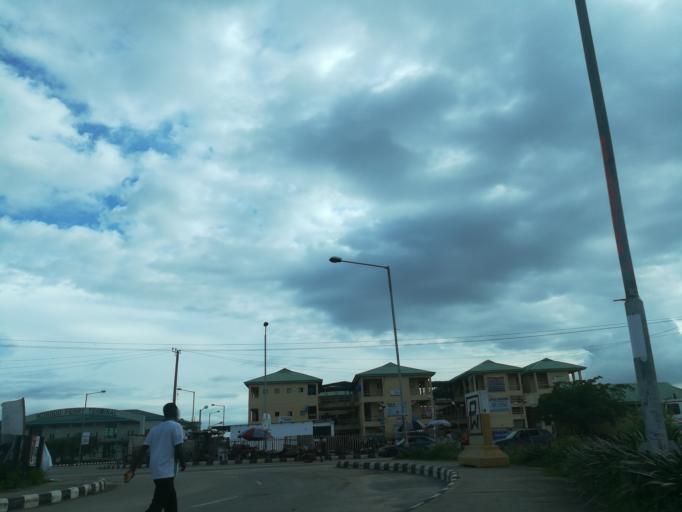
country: NG
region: Lagos
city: Ebute Ikorodu
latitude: 6.6033
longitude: 3.4861
